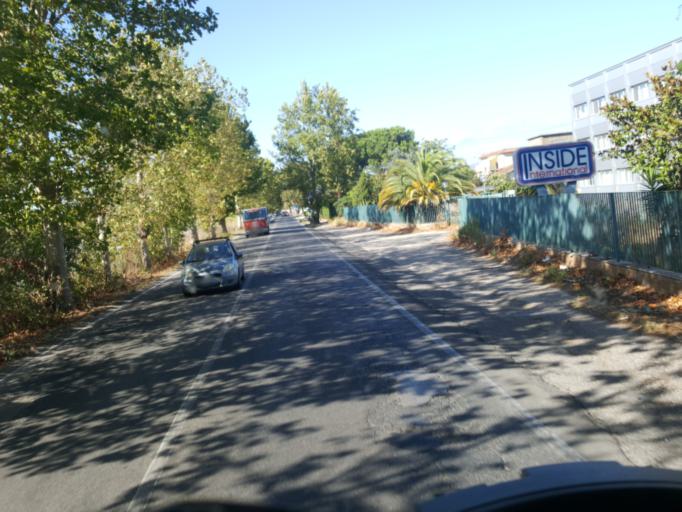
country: IT
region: Latium
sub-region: Provincia di Latina
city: Campo di Carne
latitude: 41.5483
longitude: 12.6352
